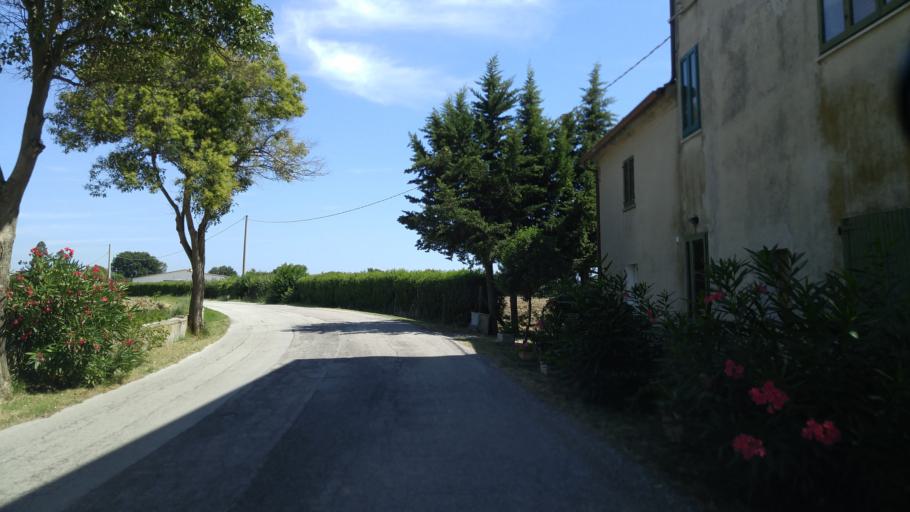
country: IT
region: The Marches
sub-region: Provincia di Pesaro e Urbino
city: Cuccurano
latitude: 43.7896
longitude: 12.9783
